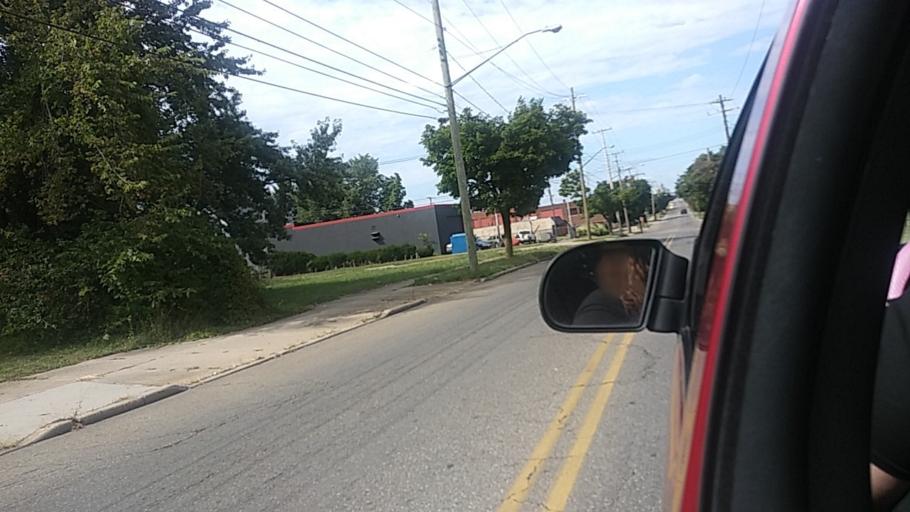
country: US
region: Ohio
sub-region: Summit County
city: Akron
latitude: 41.0558
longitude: -81.5181
